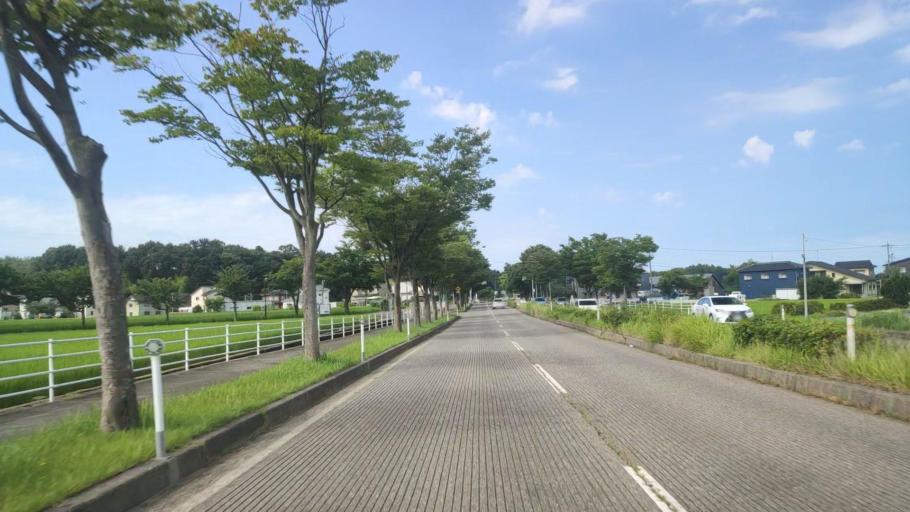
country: JP
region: Ishikawa
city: Tsurugi-asahimachi
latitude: 36.4527
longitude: 136.5719
